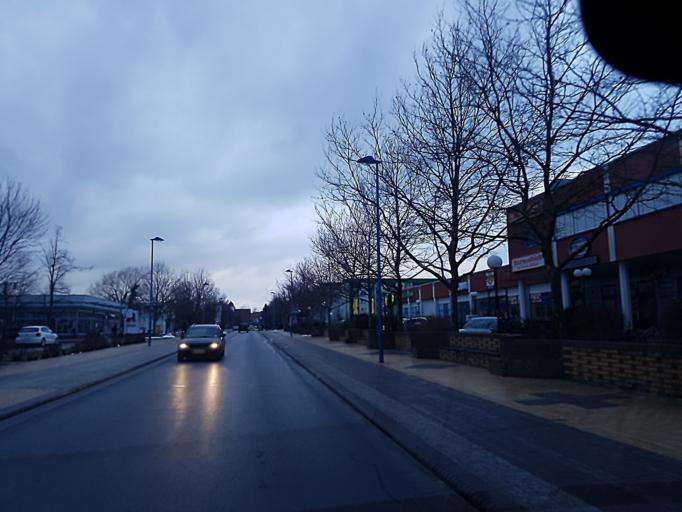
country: DE
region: Brandenburg
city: Finsterwalde
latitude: 51.6233
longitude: 13.7092
